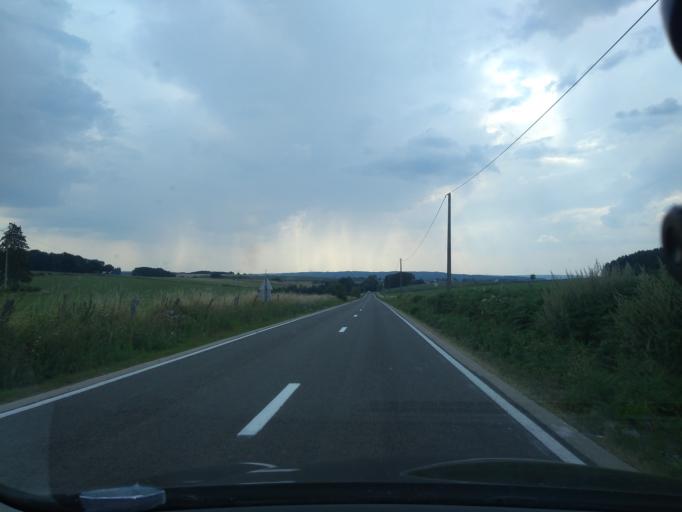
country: BE
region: Wallonia
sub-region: Province du Luxembourg
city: Bertogne
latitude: 50.0815
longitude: 5.6965
